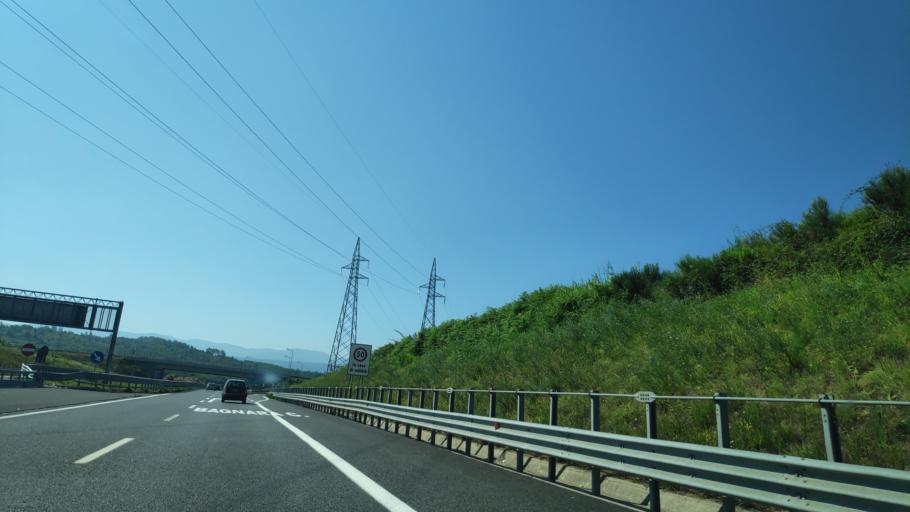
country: IT
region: Calabria
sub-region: Provincia di Reggio Calabria
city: Ceramida-Pellegrina
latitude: 38.3179
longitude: 15.8422
